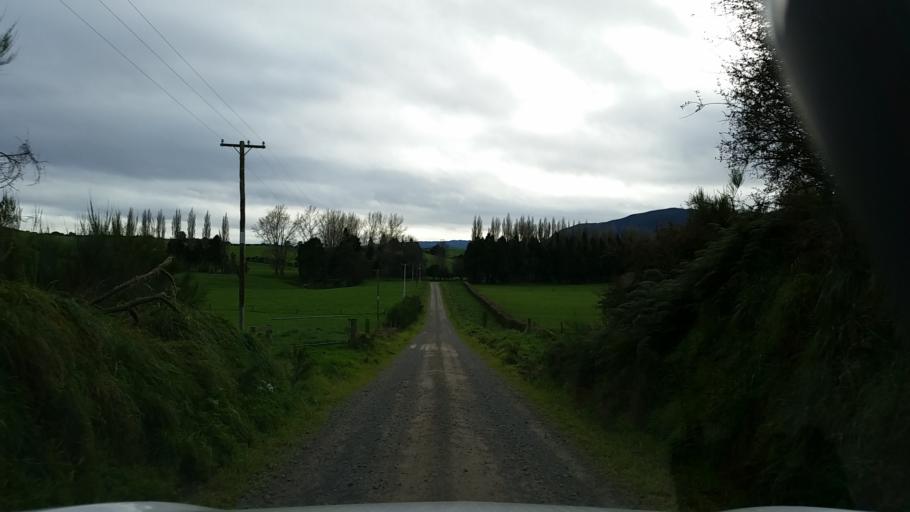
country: NZ
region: Bay of Plenty
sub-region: Rotorua District
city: Rotorua
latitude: -38.3074
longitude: 176.4688
